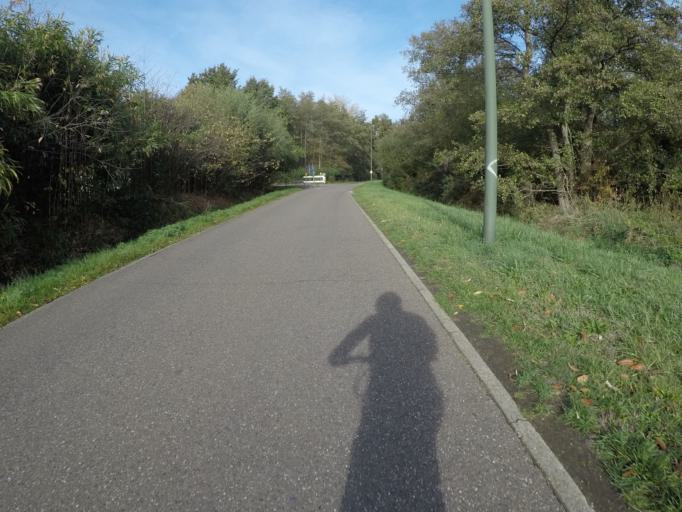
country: BE
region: Flanders
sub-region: Provincie Vlaams-Brabant
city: Begijnendijk
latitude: 51.0101
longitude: 4.7932
